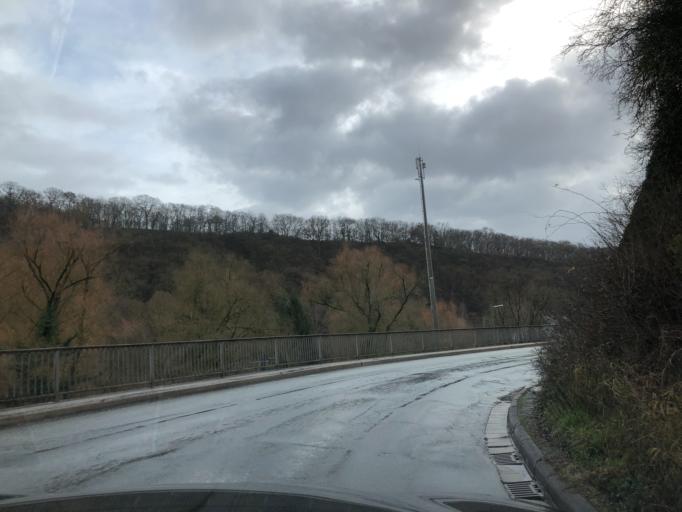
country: DE
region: Hesse
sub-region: Regierungsbezirk Giessen
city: Lohnberg
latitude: 50.5120
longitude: 8.2770
